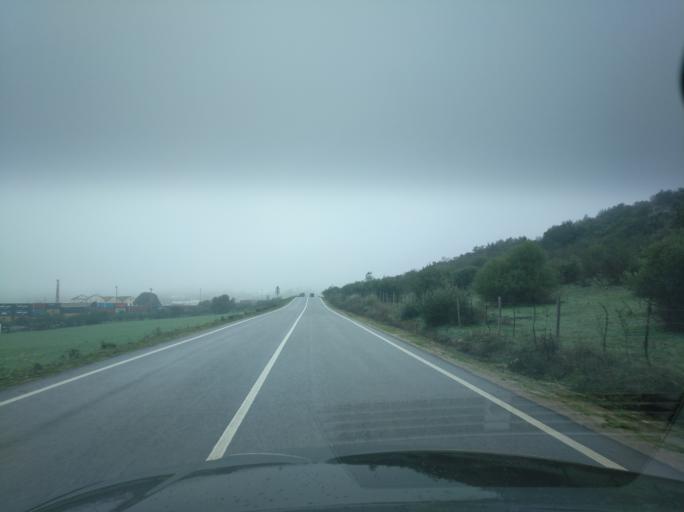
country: PT
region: Portalegre
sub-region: Elvas
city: Elvas
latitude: 38.8982
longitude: -7.1415
